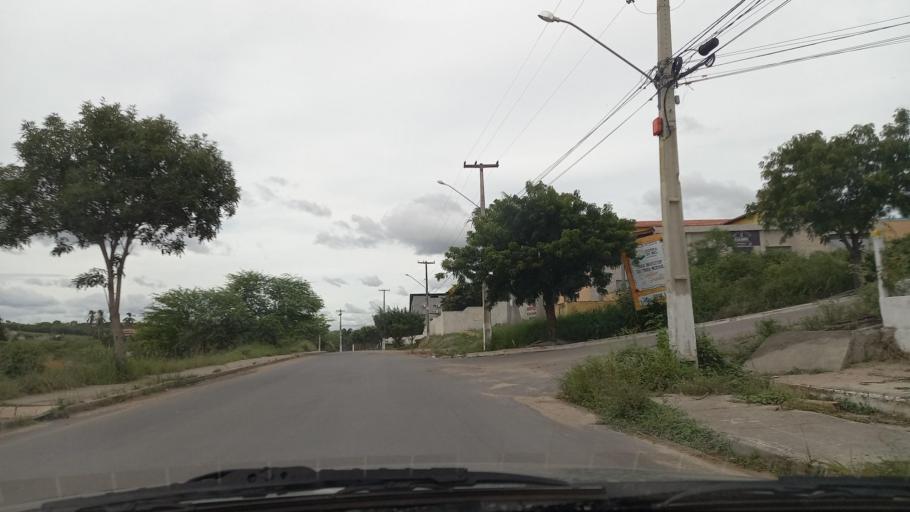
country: BR
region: Pernambuco
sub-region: Gravata
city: Gravata
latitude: -8.2120
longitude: -35.6000
